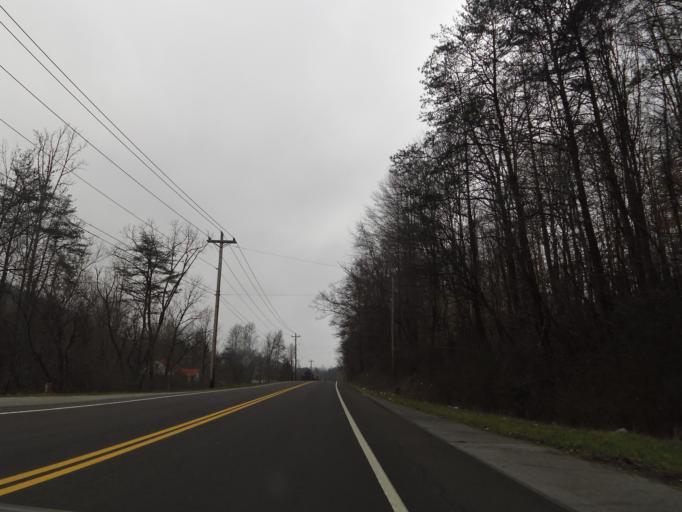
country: US
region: Tennessee
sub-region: Anderson County
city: Rocky Top
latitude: 36.1632
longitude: -84.1443
